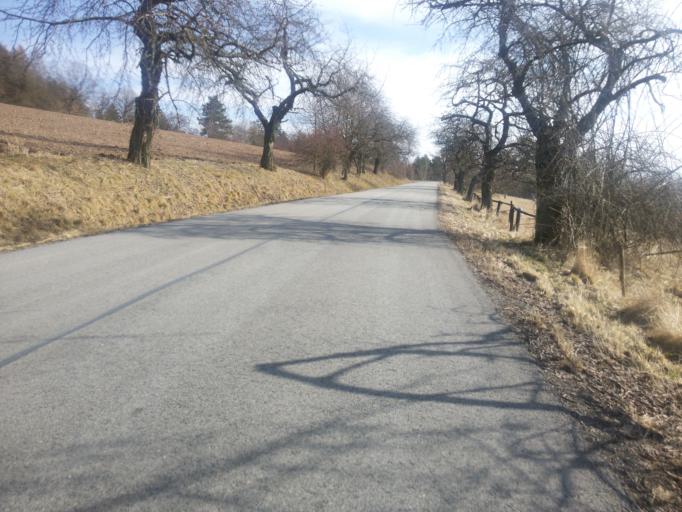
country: CZ
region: South Moravian
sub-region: Okres Brno-Venkov
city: Lomnice
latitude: 49.4195
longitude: 16.4043
